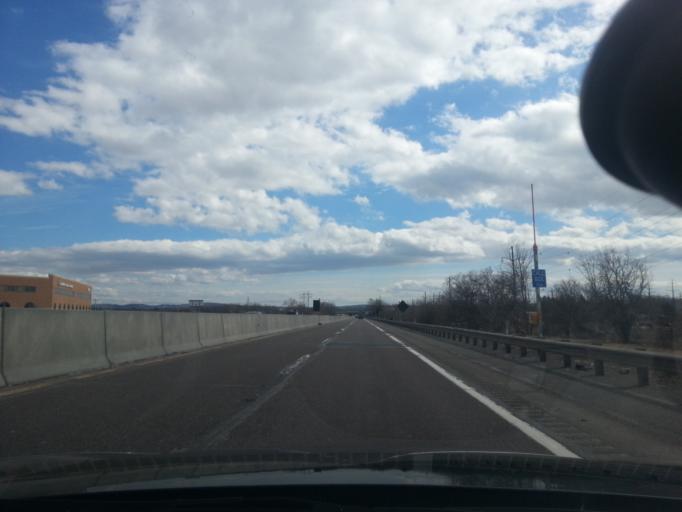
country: US
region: Pennsylvania
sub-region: Lehigh County
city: Wescosville
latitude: 40.5848
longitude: -75.5621
